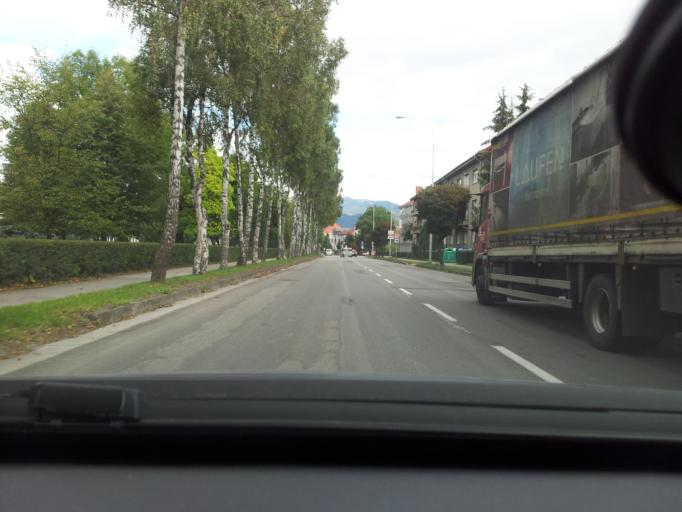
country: SK
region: Zilinsky
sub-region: Okres Martin
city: Martin
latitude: 49.0632
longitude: 18.9247
